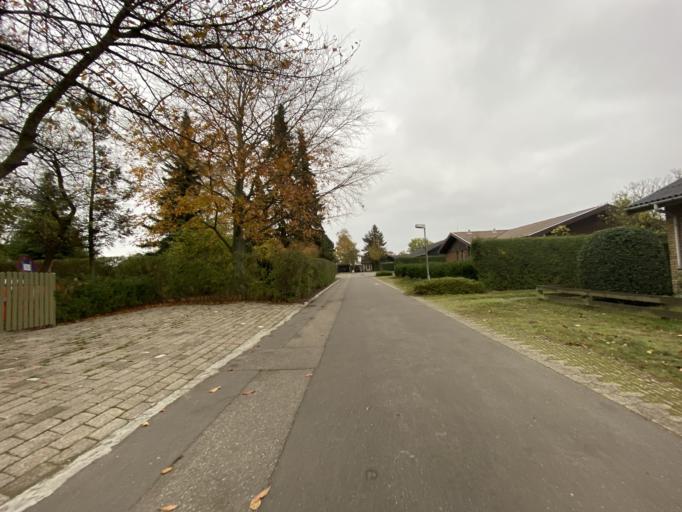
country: DK
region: Capital Region
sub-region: Dragor Kommune
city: Dragor
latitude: 55.5920
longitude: 12.6479
